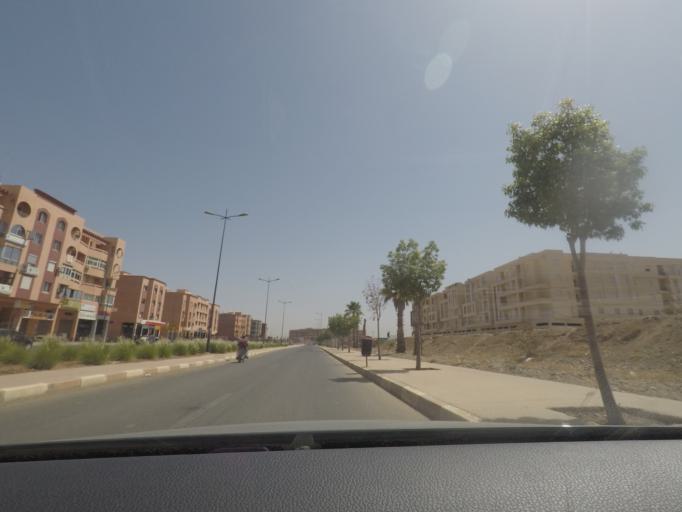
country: MA
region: Marrakech-Tensift-Al Haouz
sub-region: Marrakech
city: Marrakesh
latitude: 31.5879
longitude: -8.0384
